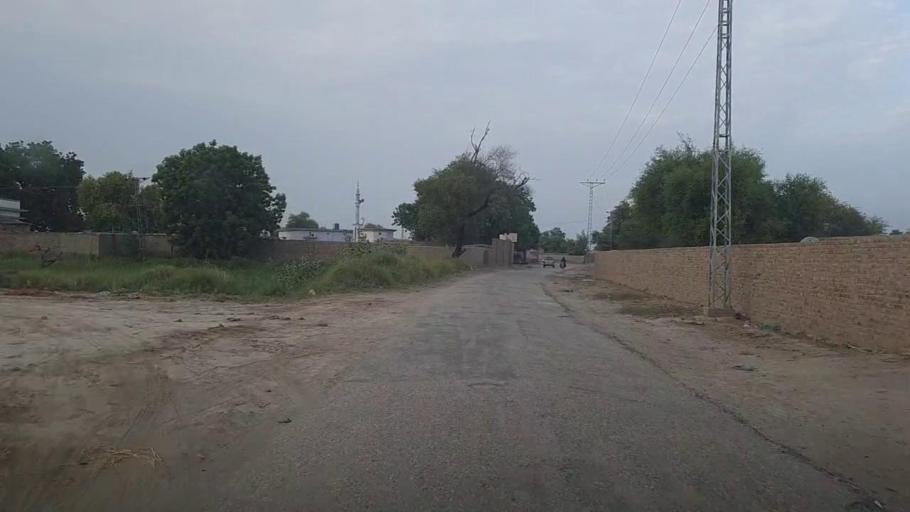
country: PK
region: Sindh
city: Kashmor
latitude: 28.3637
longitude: 69.7683
